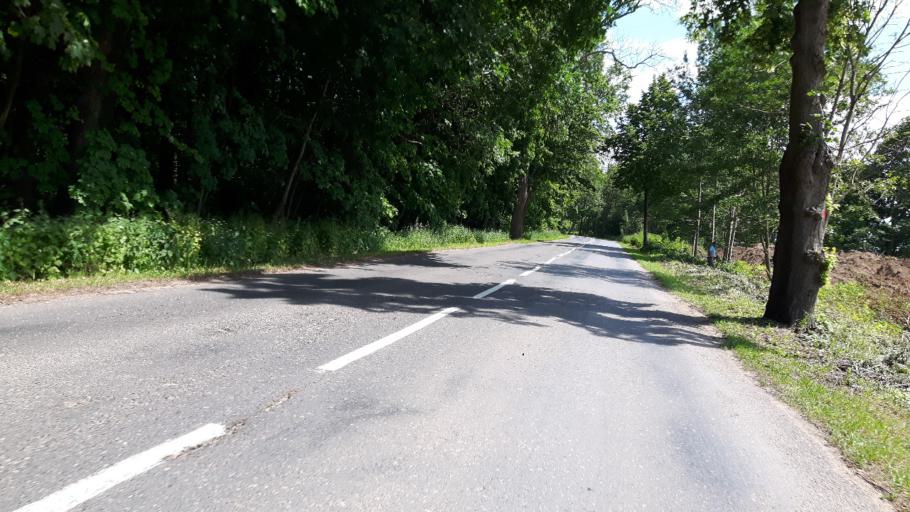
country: PL
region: Pomeranian Voivodeship
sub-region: Powiat gdanski
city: Cedry Wielkie
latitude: 54.3428
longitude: 18.8474
